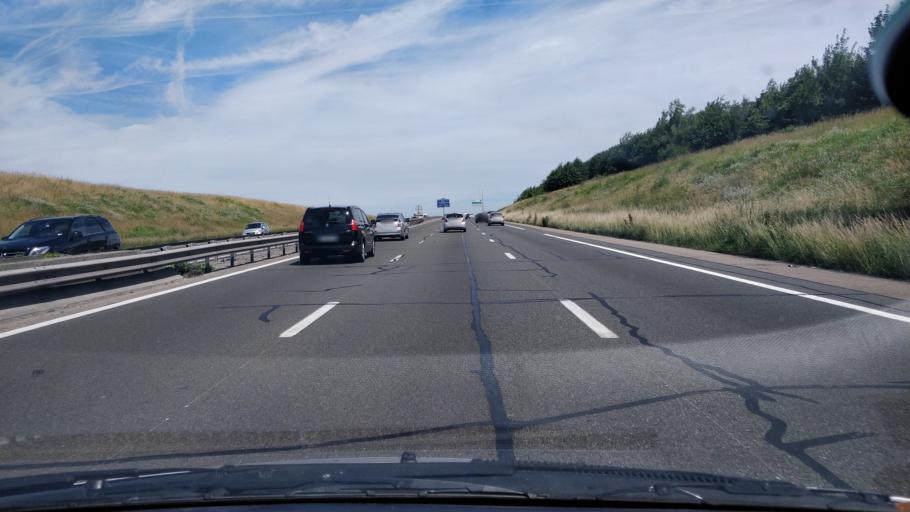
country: FR
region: Ile-de-France
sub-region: Departement de Seine-et-Marne
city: Bussy-Saint-Georges
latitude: 48.8303
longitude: 2.6951
